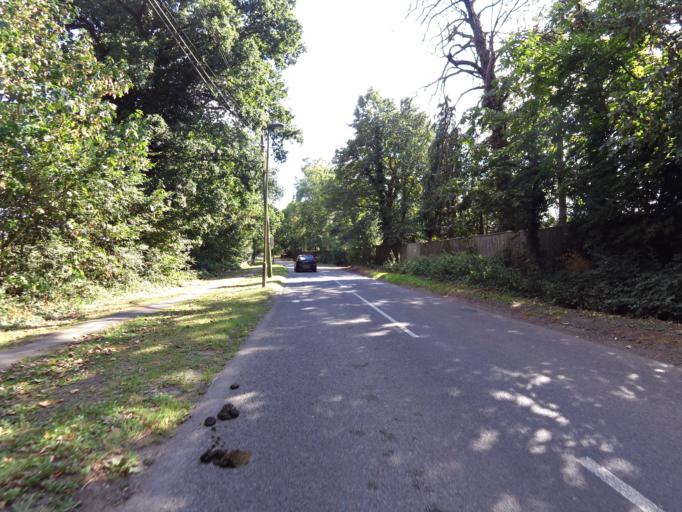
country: GB
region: England
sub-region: Greater London
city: High Barnet
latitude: 51.6596
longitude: -0.2285
